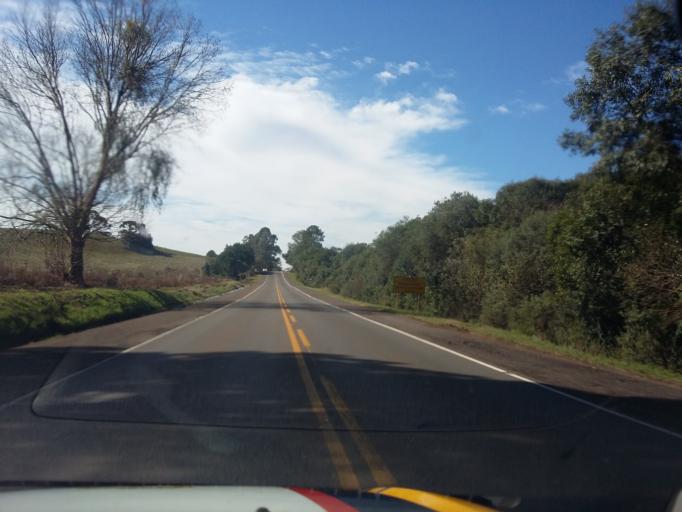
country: BR
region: Rio Grande do Sul
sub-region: Vacaria
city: Vacaria
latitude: -28.5622
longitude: -50.9925
